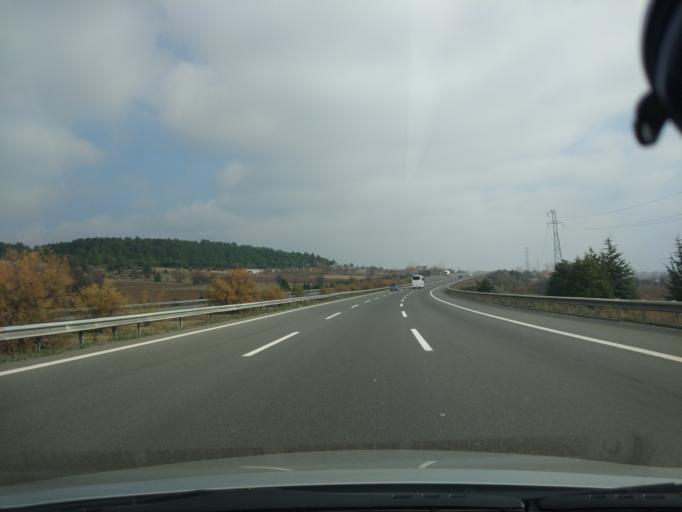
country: TR
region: Bolu
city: Bolu
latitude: 40.7623
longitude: 31.6034
